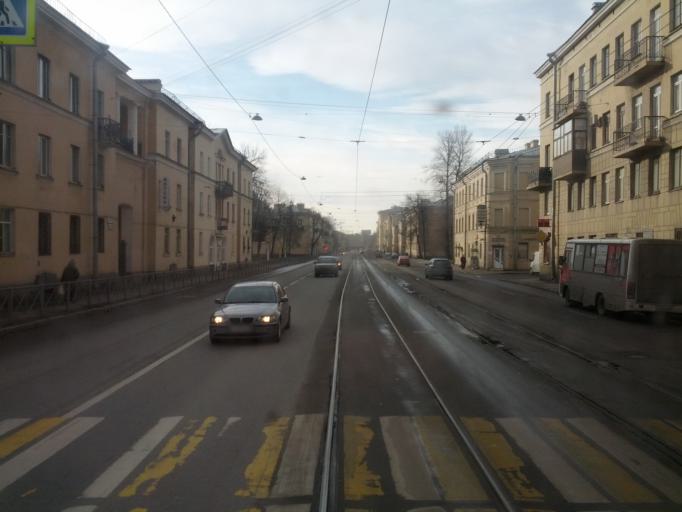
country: RU
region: Leningrad
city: Kalininskiy
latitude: 59.9520
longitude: 30.4149
